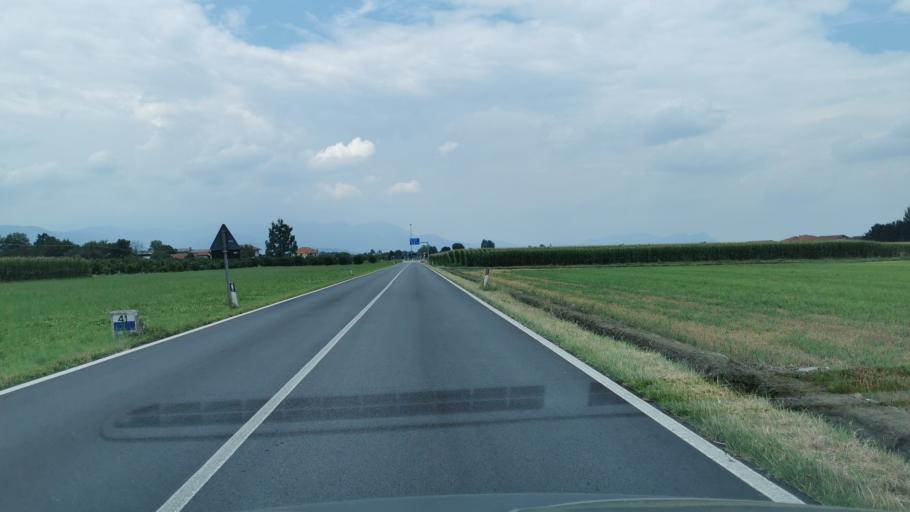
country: IT
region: Piedmont
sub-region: Provincia di Torino
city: Cavour
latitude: 44.8129
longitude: 7.3718
